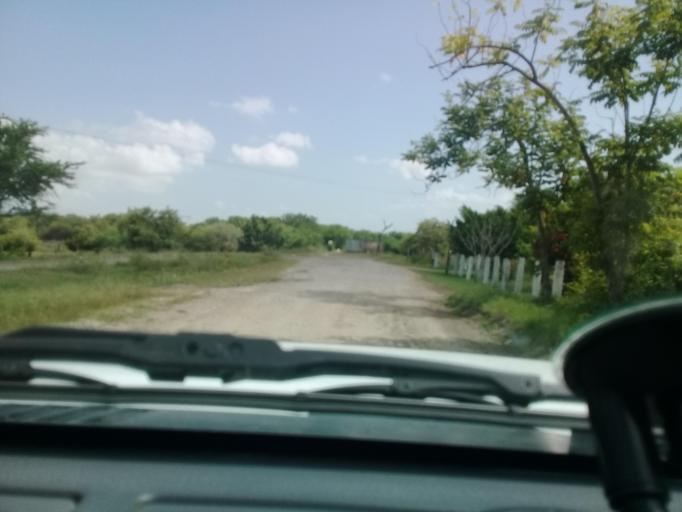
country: MX
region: Veracruz
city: Moralillo
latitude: 22.1765
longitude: -97.9489
